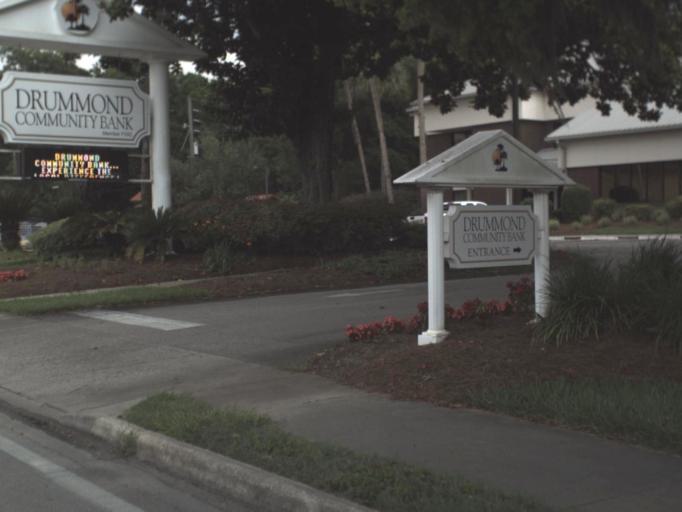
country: US
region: Florida
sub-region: Levy County
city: Williston
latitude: 29.3881
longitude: -82.4436
